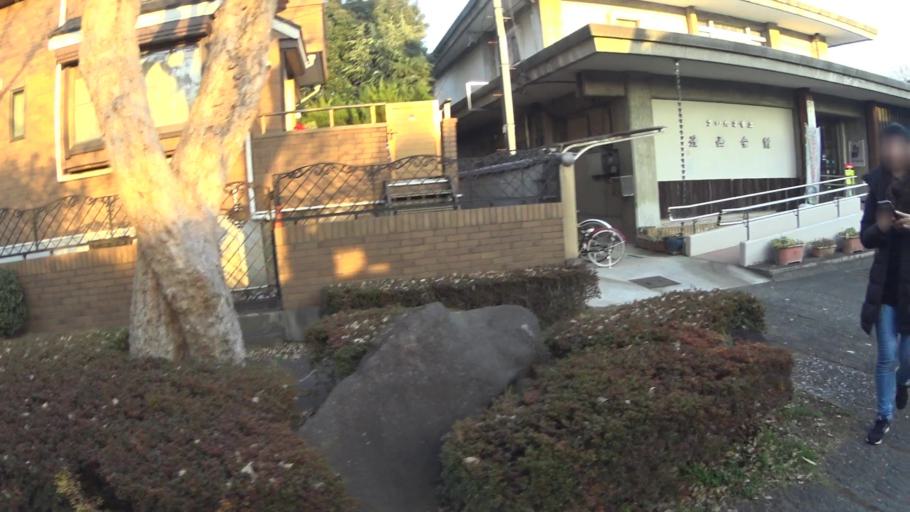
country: JP
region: Saitama
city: Saitama
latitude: 35.9264
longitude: 139.6313
